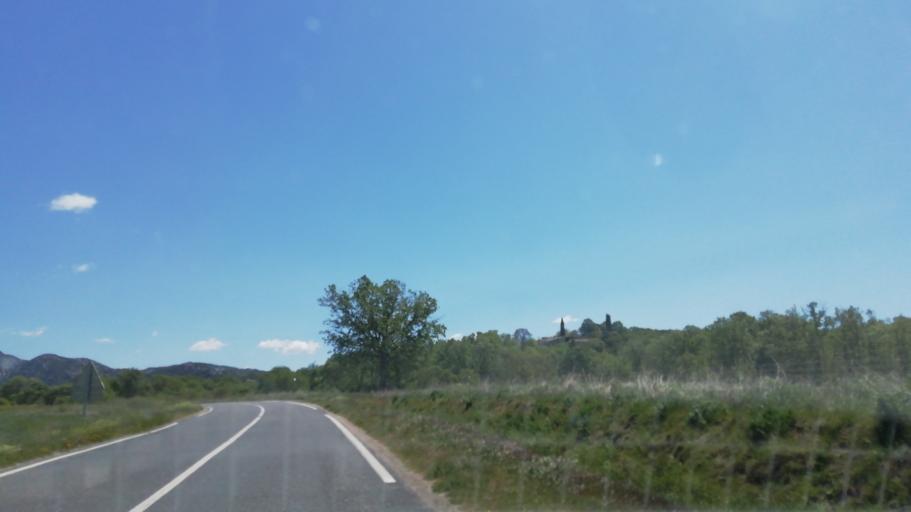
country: FR
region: Languedoc-Roussillon
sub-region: Departement de l'Herault
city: Saint-Martin-de-Londres
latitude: 43.7846
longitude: 3.7491
